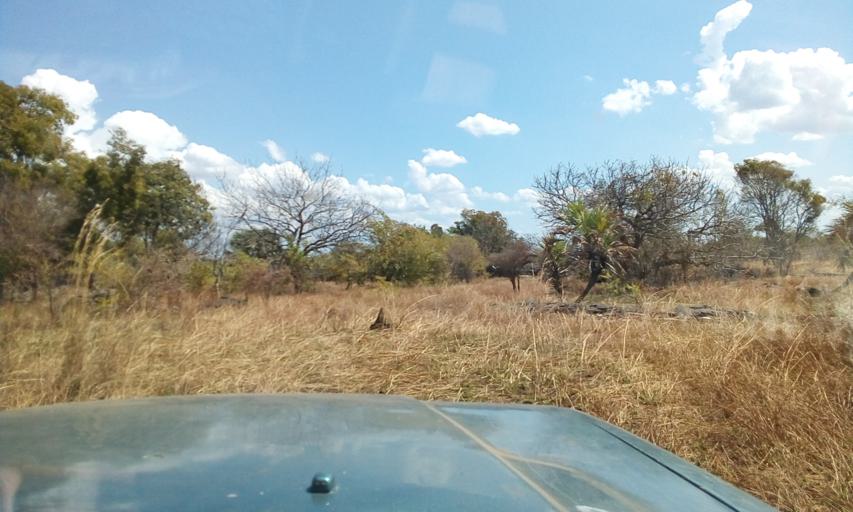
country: MG
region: Melaky
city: Mahabe
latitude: -16.4378
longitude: 45.3772
